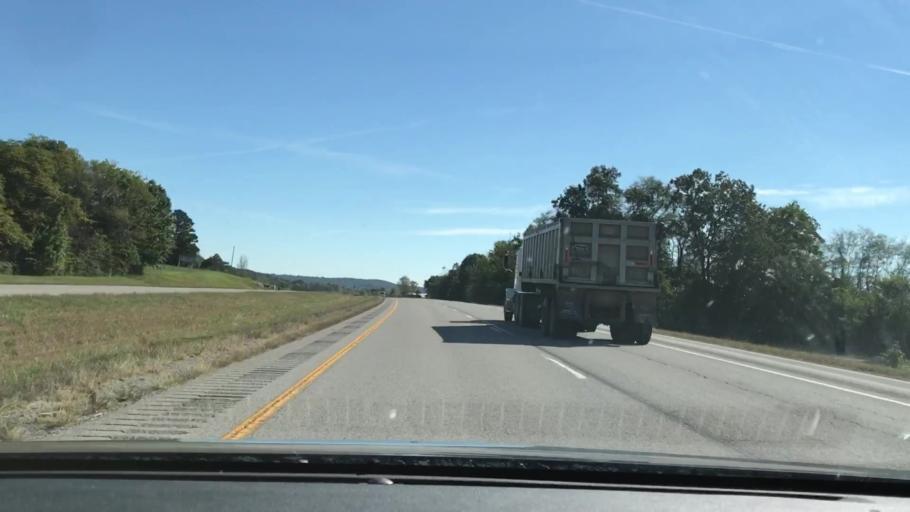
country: US
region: Kentucky
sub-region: Todd County
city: Elkton
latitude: 36.8460
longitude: -87.2921
